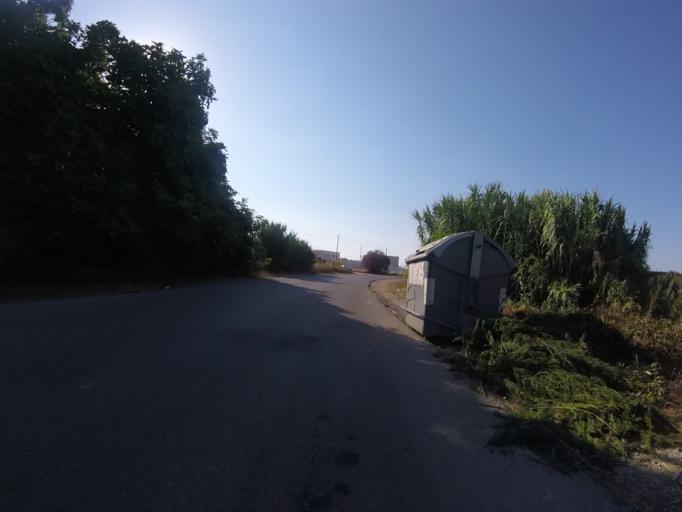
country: ES
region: Valencia
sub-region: Provincia de Castello
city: Benicarlo
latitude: 40.4234
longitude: 0.4342
